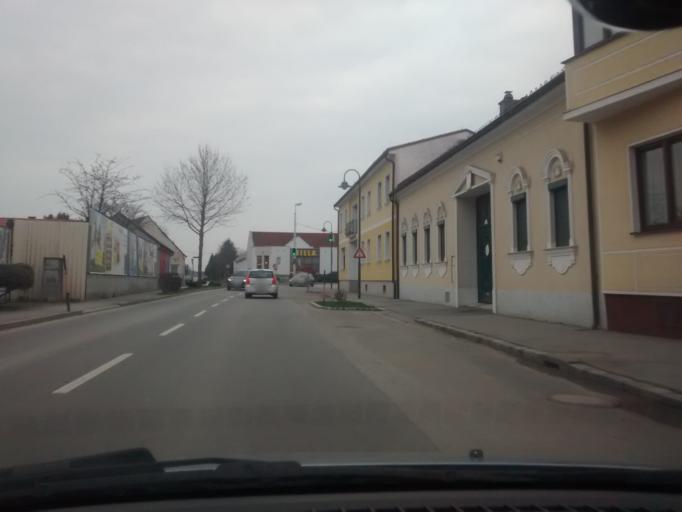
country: AT
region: Lower Austria
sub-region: Politischer Bezirk Wien-Umgebung
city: Gramatneusiedl
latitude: 48.0278
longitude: 16.4870
